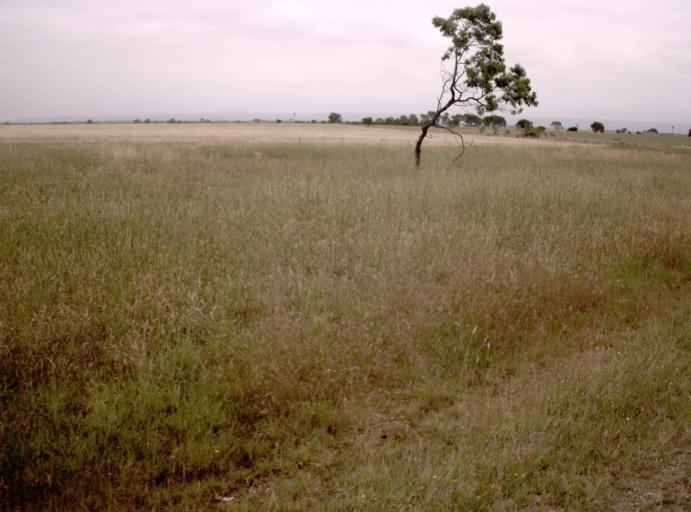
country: AU
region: Victoria
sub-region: Wellington
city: Heyfield
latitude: -38.1167
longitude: 146.7763
